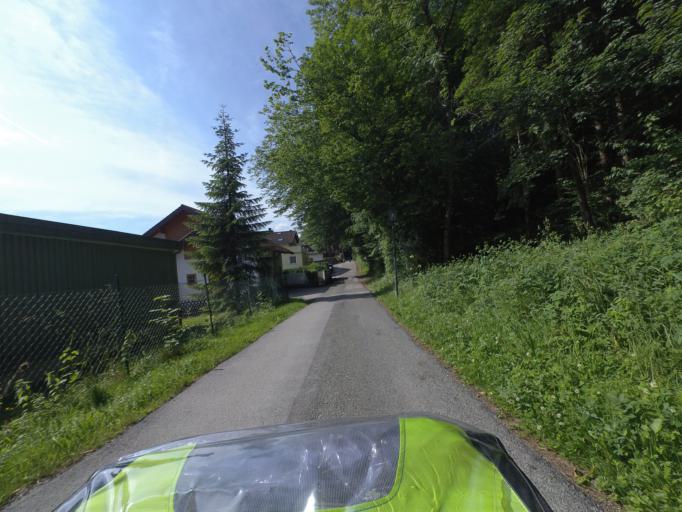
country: AT
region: Salzburg
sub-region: Politischer Bezirk Salzburg-Umgebung
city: Grodig
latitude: 47.7313
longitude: 13.0366
